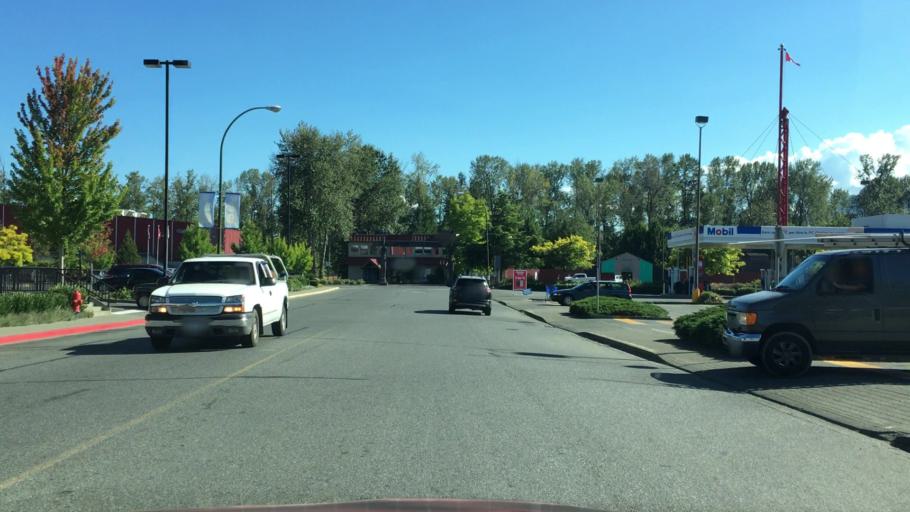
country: CA
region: British Columbia
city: Duncan
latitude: 48.7746
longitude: -123.7017
